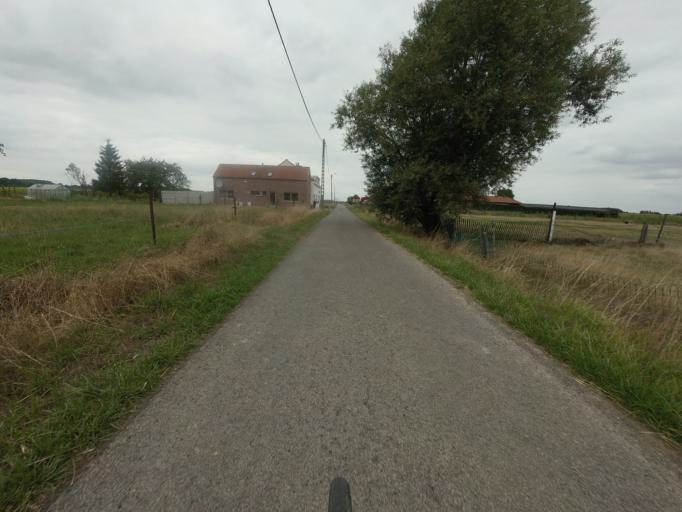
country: BE
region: Flanders
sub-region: Provincie Vlaams-Brabant
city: Herent
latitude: 50.9199
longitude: 4.6258
